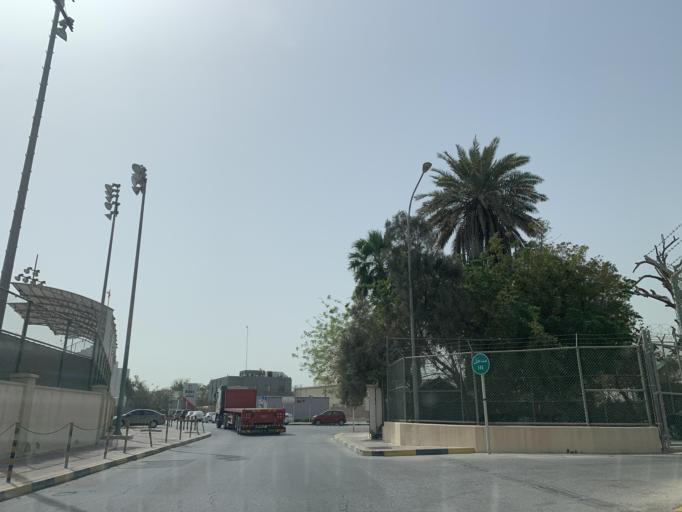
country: BH
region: Manama
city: Manama
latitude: 26.2079
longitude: 50.6056
